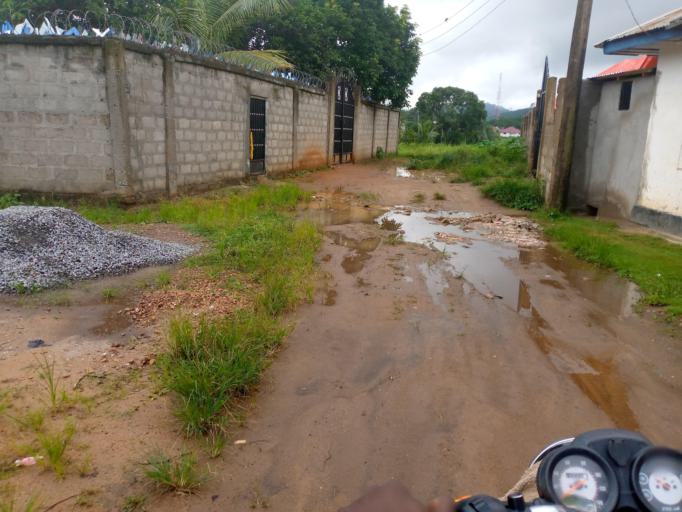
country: SL
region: Eastern Province
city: Kenema
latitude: 7.8506
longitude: -11.2000
